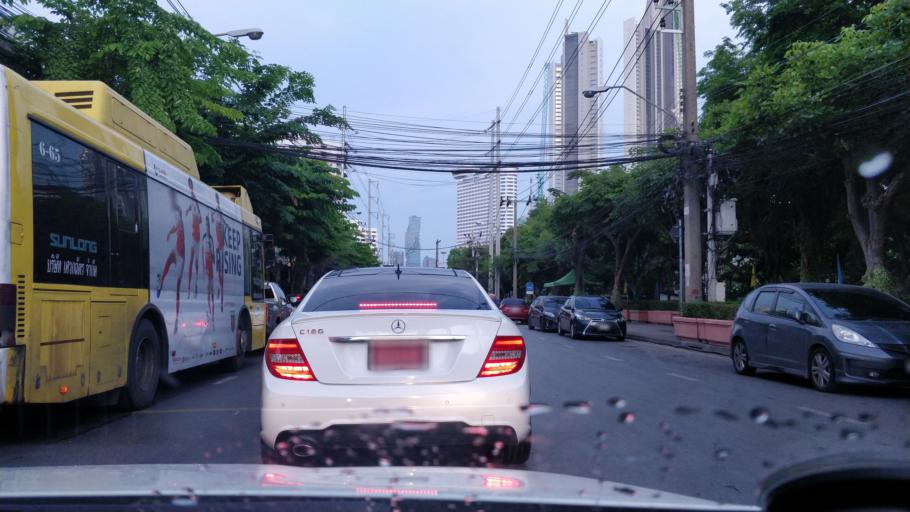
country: TH
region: Bangkok
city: Khlong San
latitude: 13.7312
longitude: 100.5054
